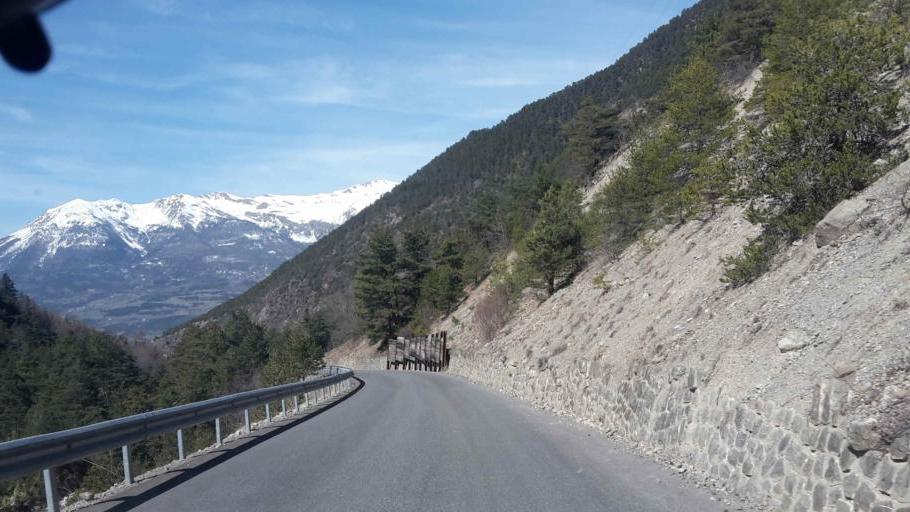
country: FR
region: Provence-Alpes-Cote d'Azur
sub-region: Departement des Hautes-Alpes
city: Embrun
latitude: 44.5532
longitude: 6.5766
